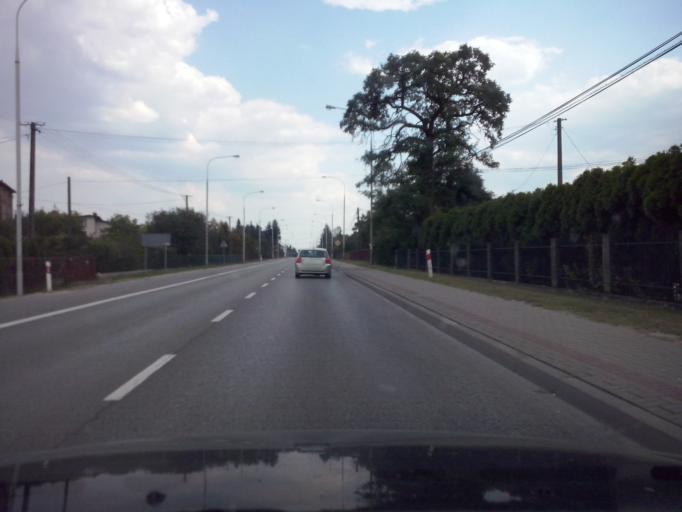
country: PL
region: Subcarpathian Voivodeship
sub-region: Powiat stalowowolski
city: Stalowa Wola
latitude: 50.5435
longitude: 22.0853
